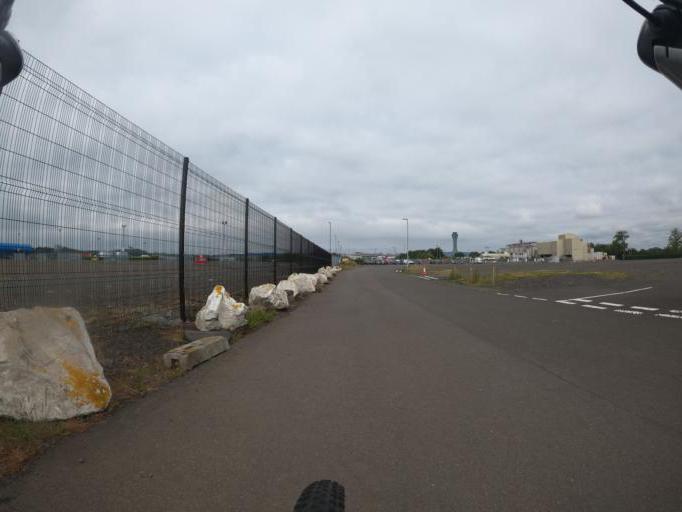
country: GB
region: Scotland
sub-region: Edinburgh
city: Ratho
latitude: 55.9449
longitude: -3.3743
